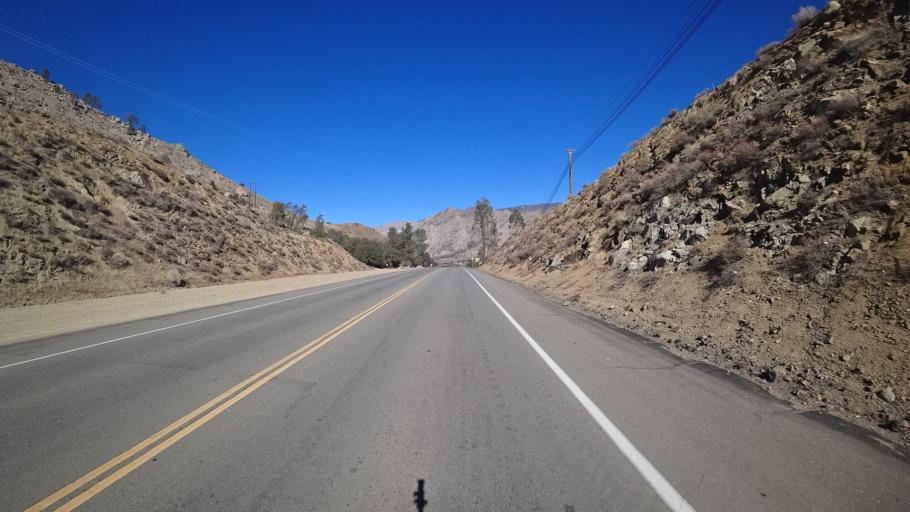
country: US
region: California
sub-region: Kern County
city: Kernville
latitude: 35.7291
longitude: -118.4300
